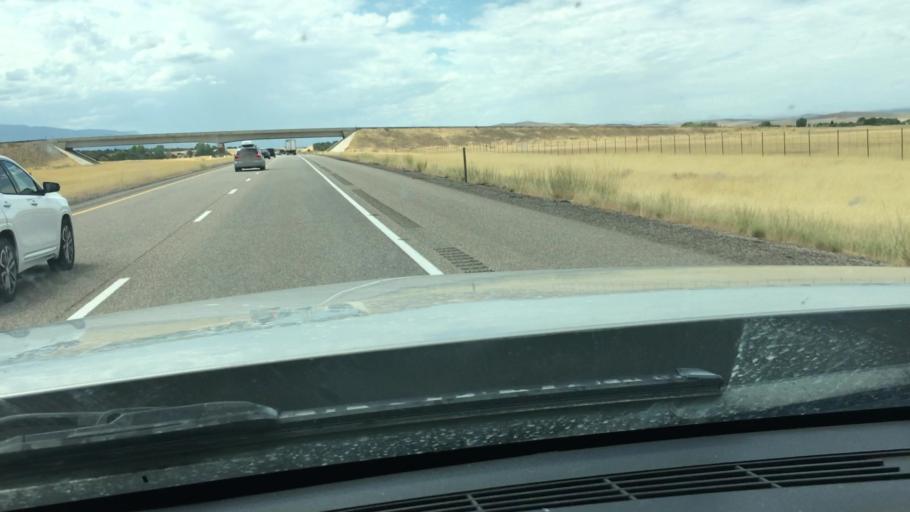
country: US
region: Utah
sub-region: Millard County
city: Fillmore
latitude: 39.1131
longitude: -112.2527
